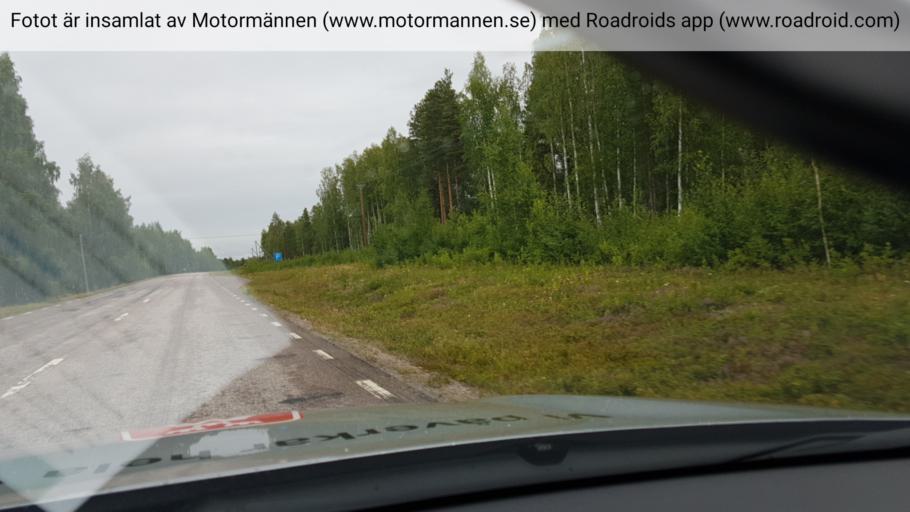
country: SE
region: Norrbotten
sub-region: Alvsbyns Kommun
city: AElvsbyn
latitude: 66.1837
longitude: 20.8788
